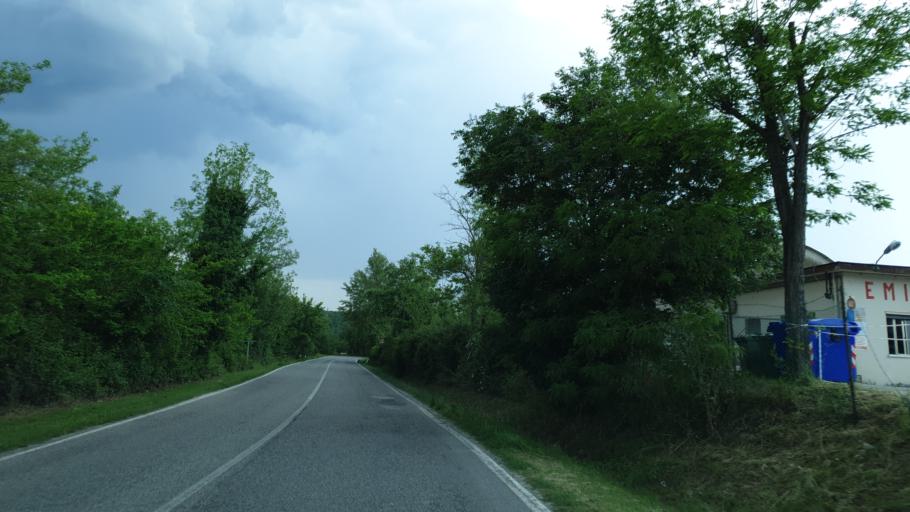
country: IT
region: Emilia-Romagna
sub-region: Provincia di Rimini
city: Secchiano
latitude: 43.9124
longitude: 12.3042
